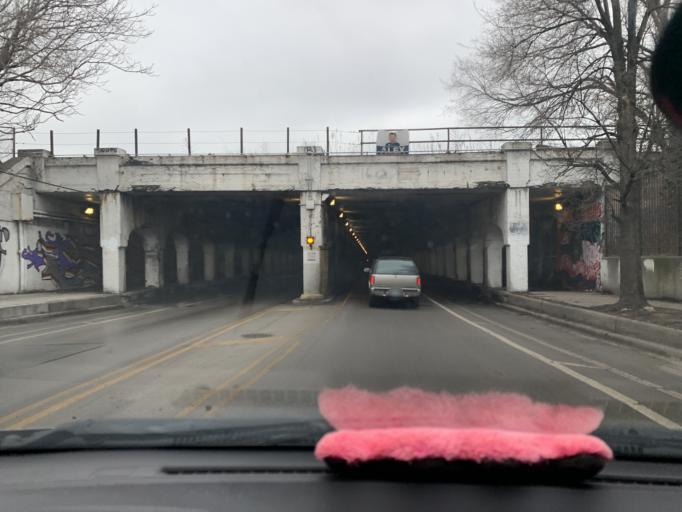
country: US
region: Illinois
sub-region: Cook County
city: Chicago
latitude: 41.8589
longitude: -87.6760
